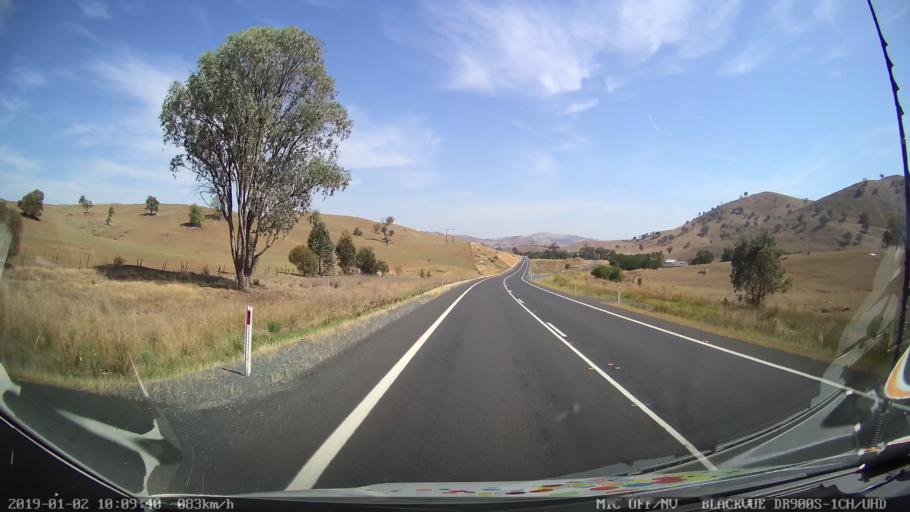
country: AU
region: New South Wales
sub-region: Gundagai
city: Gundagai
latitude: -35.1142
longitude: 148.0979
